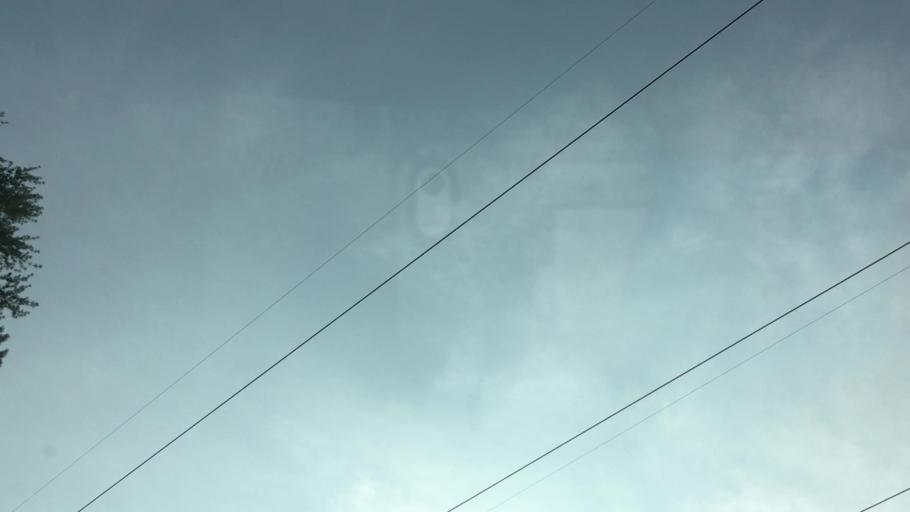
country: US
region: Alabama
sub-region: Bibb County
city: Woodstock
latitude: 33.2156
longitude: -87.0761
